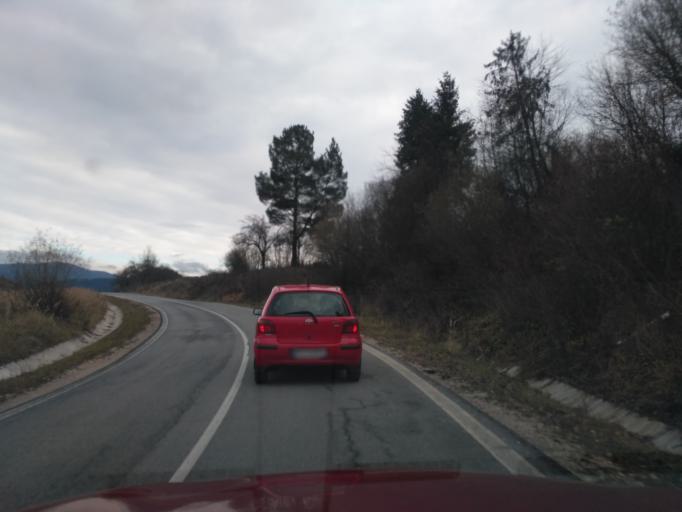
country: SK
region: Kosicky
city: Krompachy
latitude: 48.8021
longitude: 20.7310
